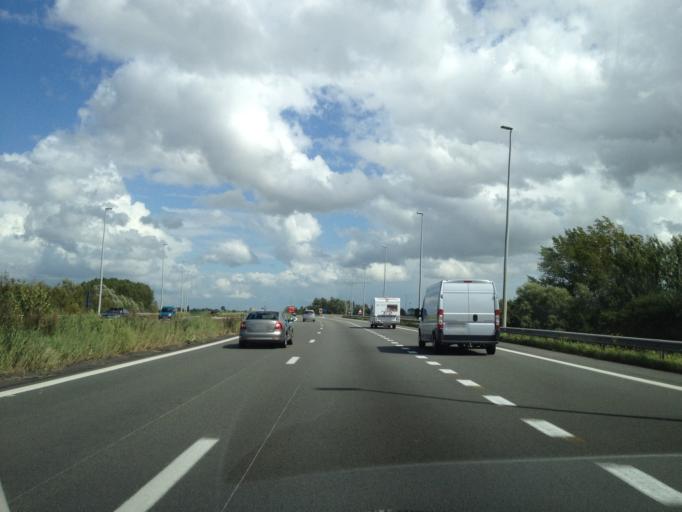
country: BE
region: Flanders
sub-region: Provincie West-Vlaanderen
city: Veurne
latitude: 51.0562
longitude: 2.6594
